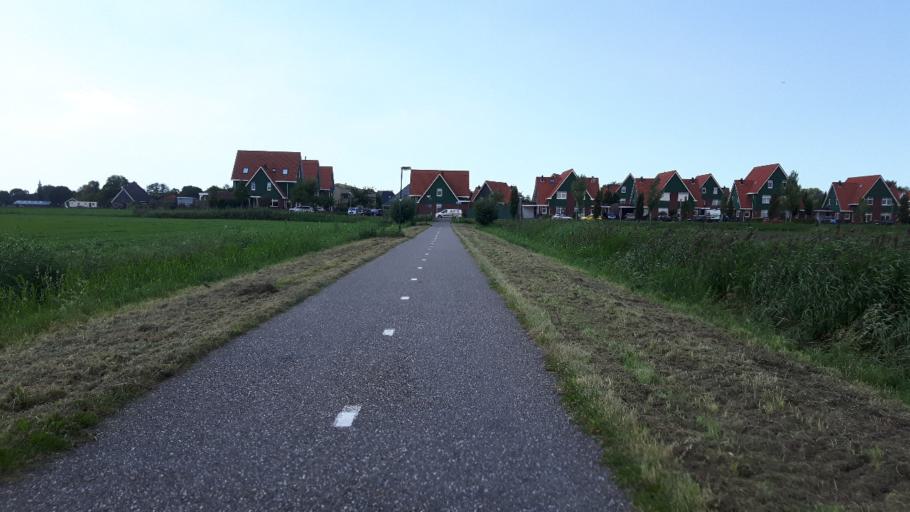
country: NL
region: North Holland
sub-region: Gemeente Medemblik
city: Opperdoes
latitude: 52.7172
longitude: 5.0833
